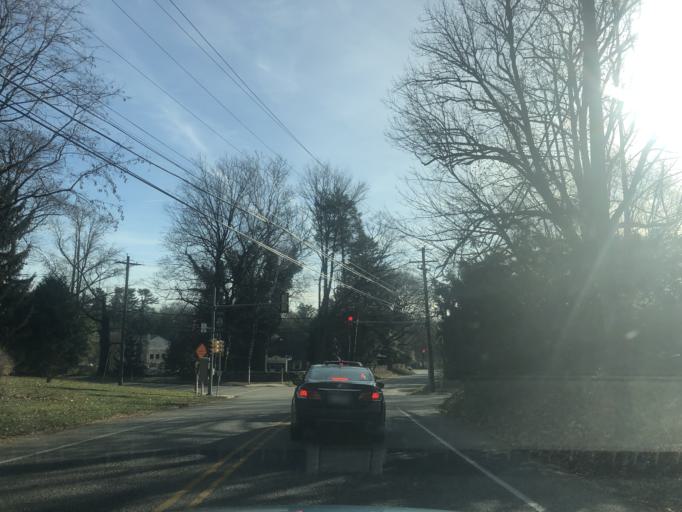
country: US
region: Pennsylvania
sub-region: Delaware County
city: Radnor
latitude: 40.0279
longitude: -75.3535
